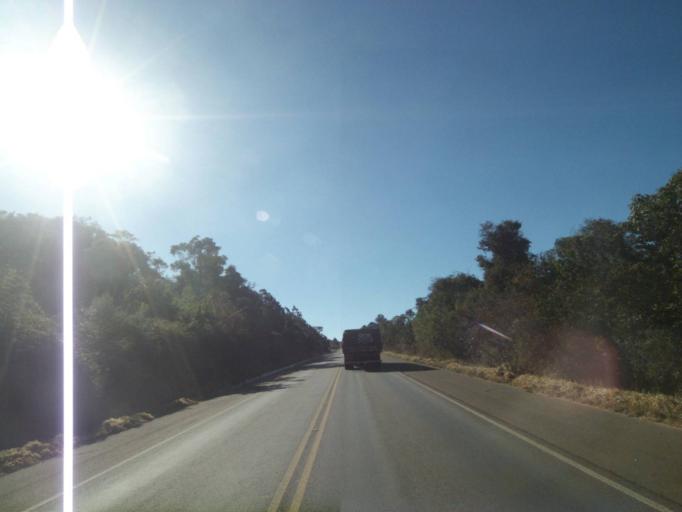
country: BR
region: Parana
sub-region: Tibagi
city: Tibagi
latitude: -24.6521
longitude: -50.4532
